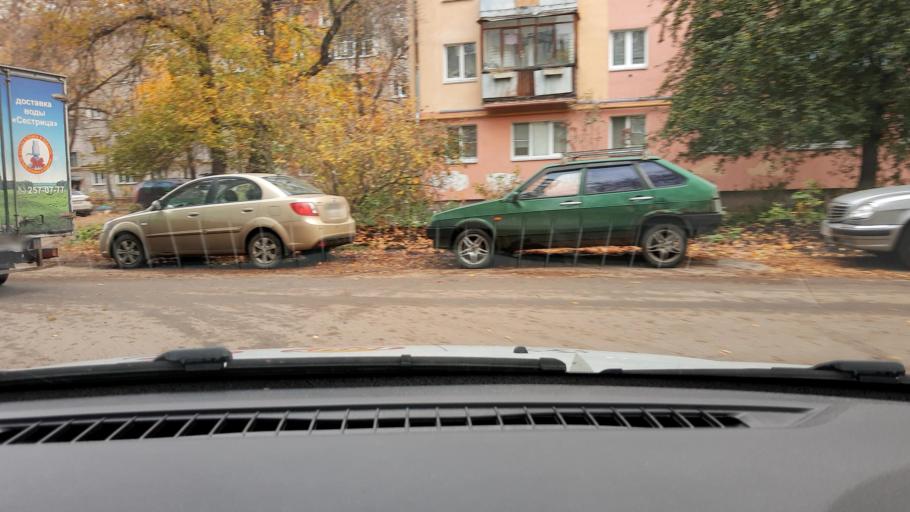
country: RU
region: Nizjnij Novgorod
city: Burevestnik
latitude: 56.2305
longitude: 43.8648
